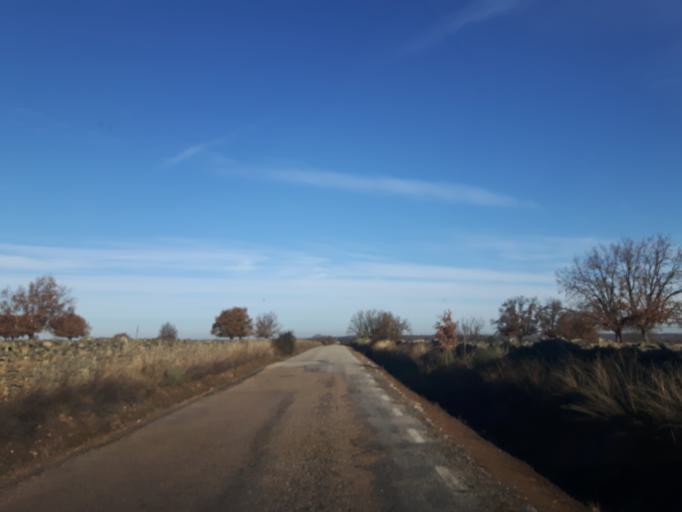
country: ES
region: Castille and Leon
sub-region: Provincia de Salamanca
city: Olmedo de Camaces
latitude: 40.9279
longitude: -6.6182
